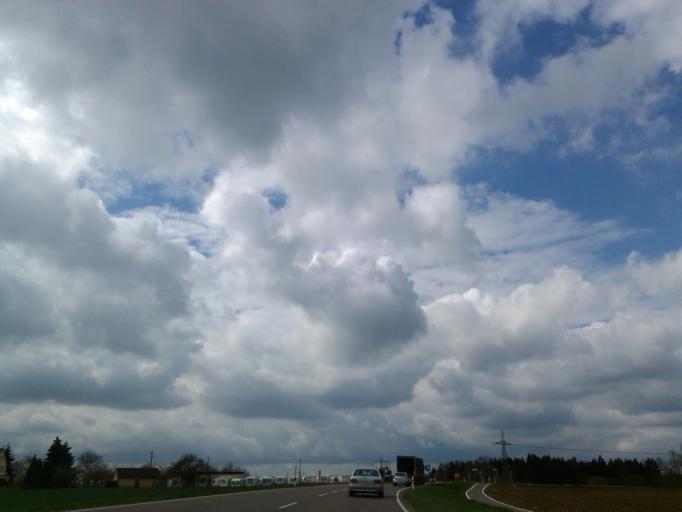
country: DE
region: Bavaria
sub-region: Swabia
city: Neu-Ulm
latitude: 48.4439
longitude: 10.0189
